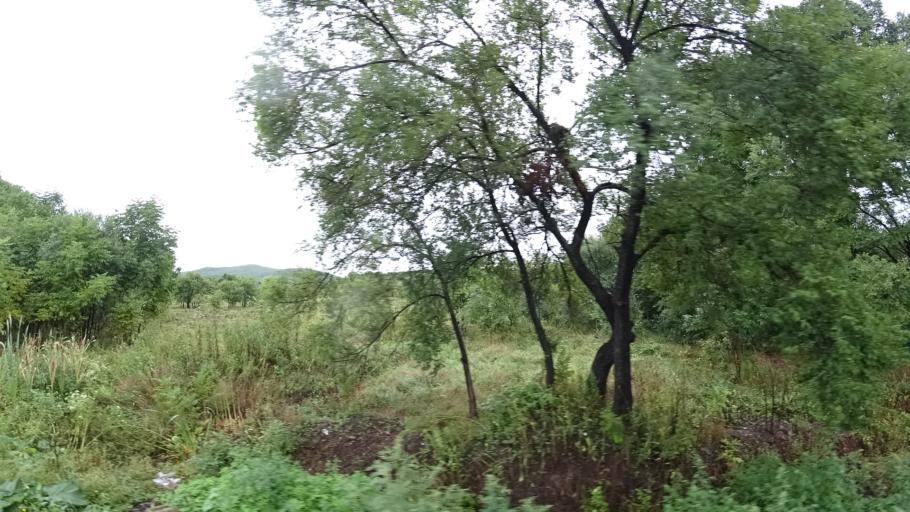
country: RU
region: Primorskiy
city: Monastyrishche
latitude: 44.2353
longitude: 132.4639
